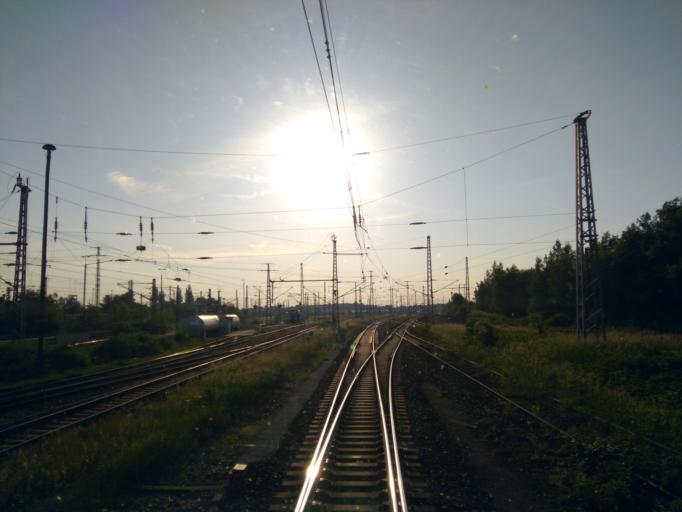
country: DE
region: Brandenburg
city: Cottbus
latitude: 51.7502
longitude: 14.3097
